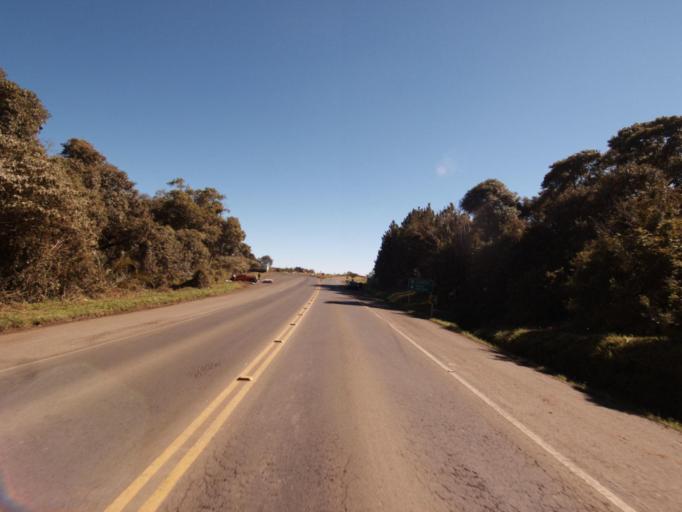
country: BR
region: Santa Catarina
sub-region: Joacaba
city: Joacaba
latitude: -27.0982
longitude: -51.6512
